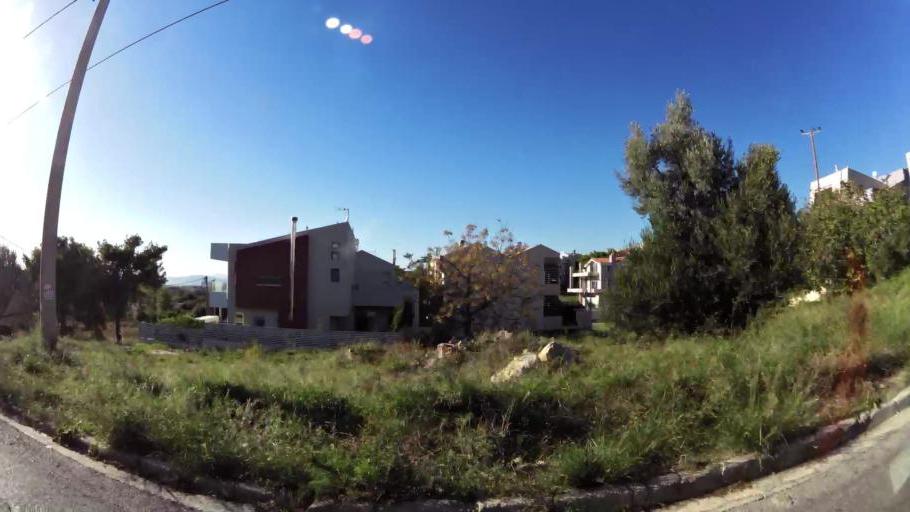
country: GR
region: Attica
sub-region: Nomarchia Athinas
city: Penteli
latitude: 38.0413
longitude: 23.8529
